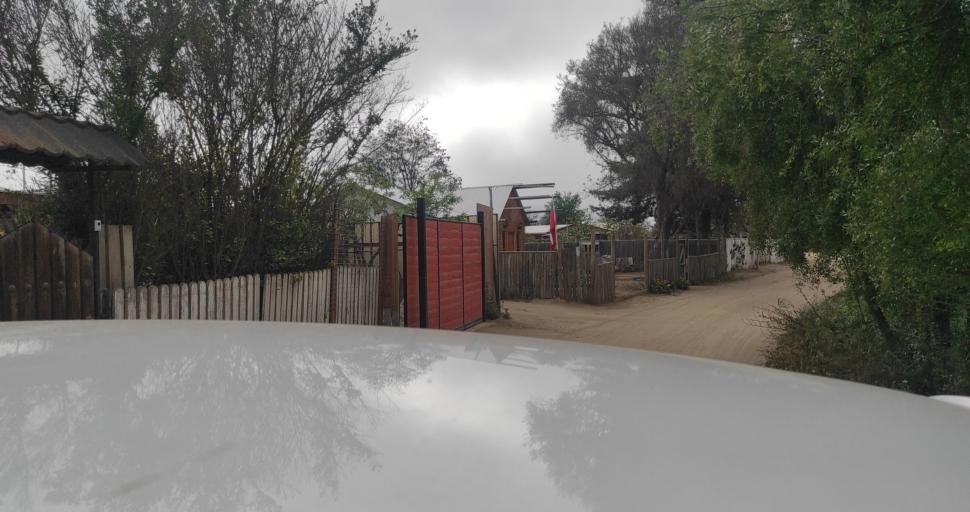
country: CL
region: Valparaiso
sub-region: Provincia de Marga Marga
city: Villa Alemana
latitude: -33.3602
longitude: -71.3063
